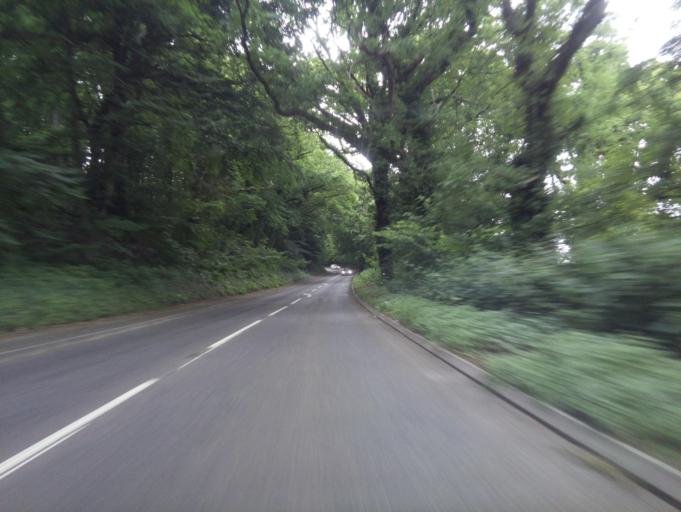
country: GB
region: England
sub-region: Dorset
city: Lyme Regis
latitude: 50.7437
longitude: -2.9221
